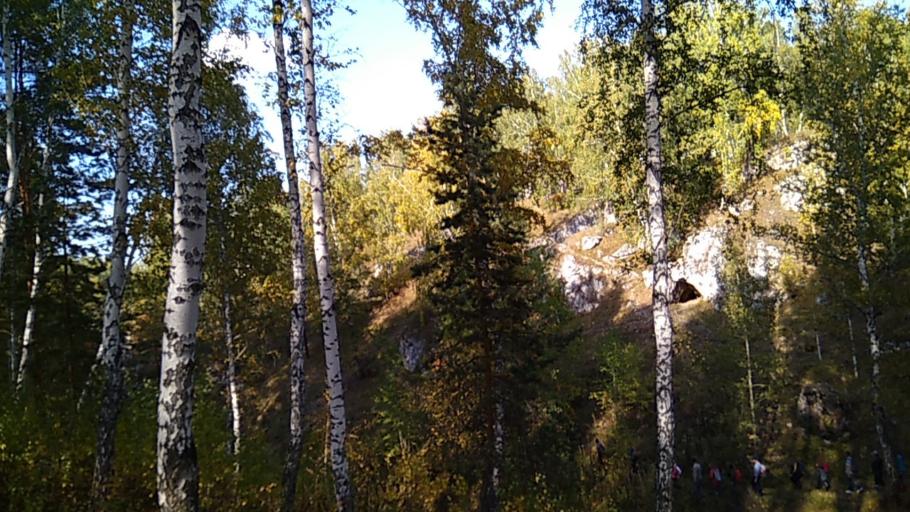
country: RU
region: Sverdlovsk
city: Pokrovskoye
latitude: 56.4284
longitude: 61.6121
